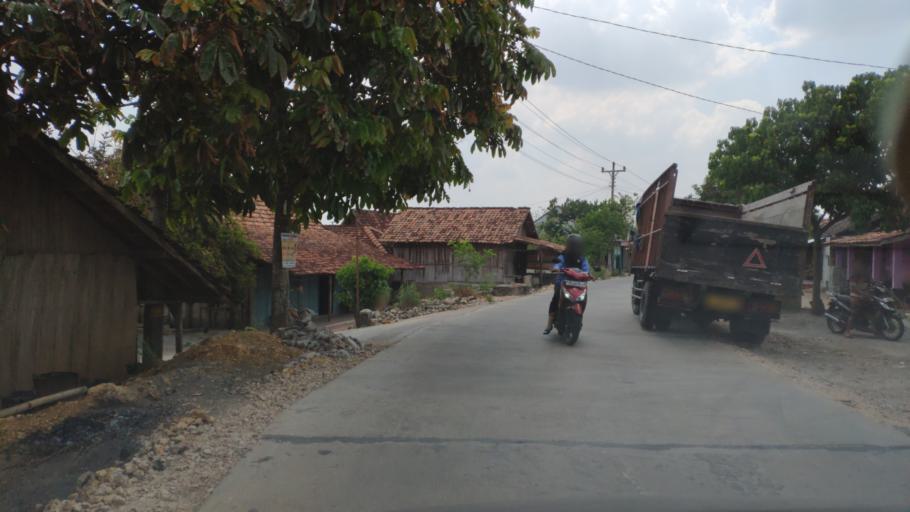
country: ID
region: Central Java
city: Ngapus
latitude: -6.9569
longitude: 111.1803
